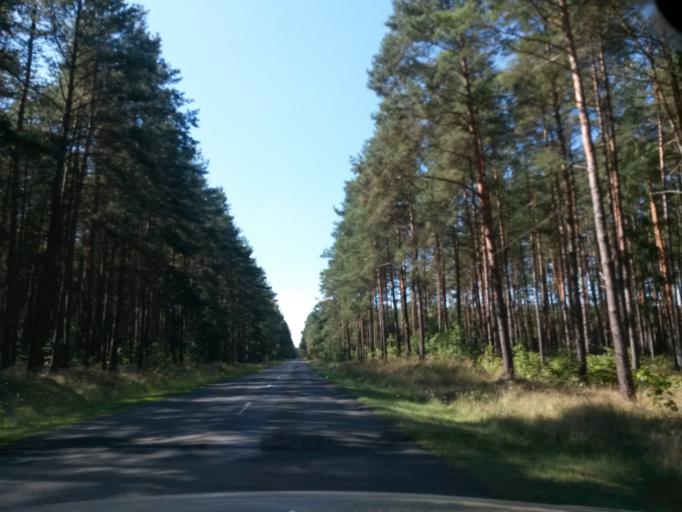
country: DE
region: Brandenburg
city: Lychen
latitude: 53.2262
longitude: 13.3631
